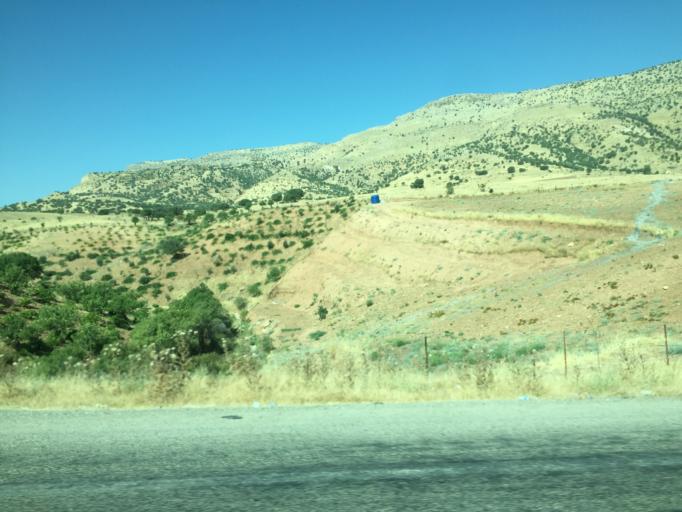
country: TR
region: Batman
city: Hasankeyf
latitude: 37.6717
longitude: 41.4553
